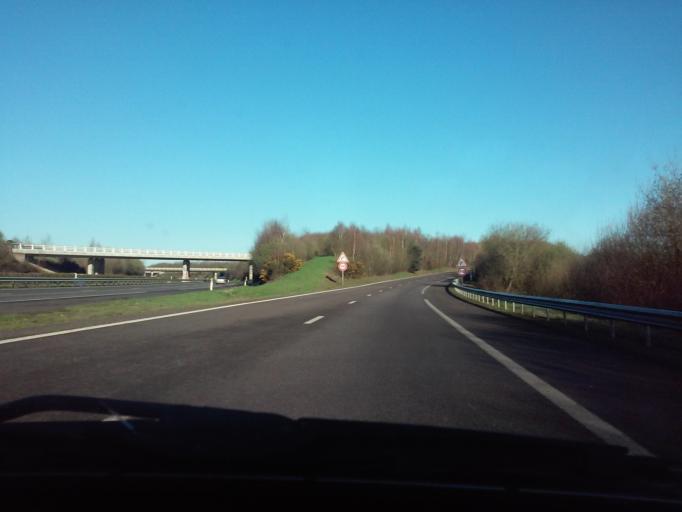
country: FR
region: Brittany
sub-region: Departement d'Ille-et-Vilaine
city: Fouillard
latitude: 48.1490
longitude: -1.5963
